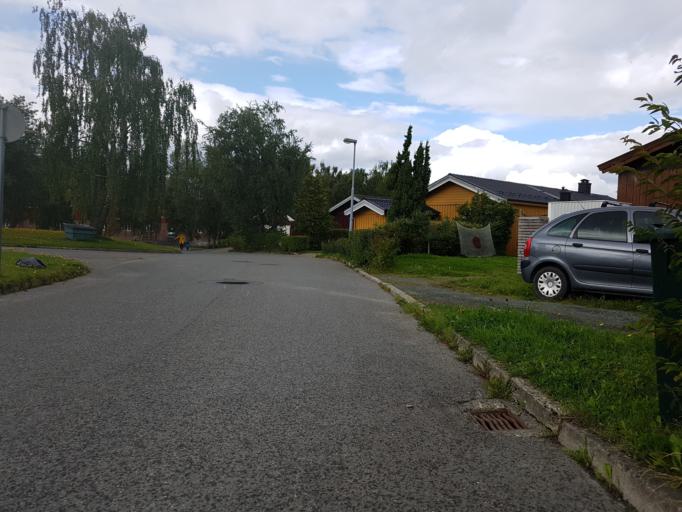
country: NO
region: Sor-Trondelag
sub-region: Trondheim
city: Trondheim
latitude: 63.4162
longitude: 10.4611
